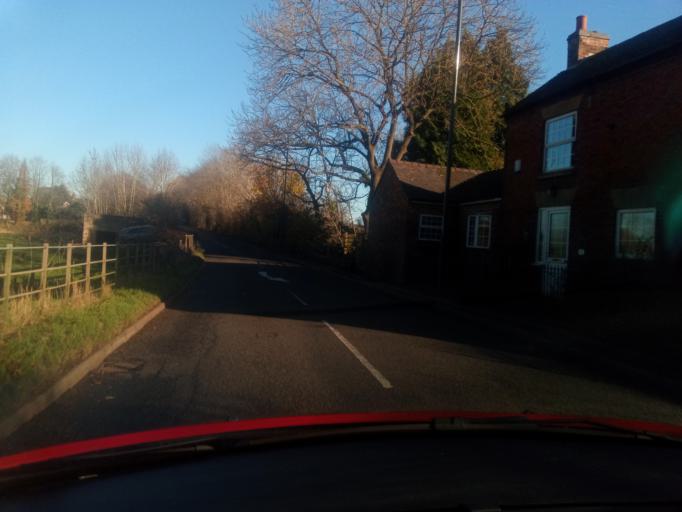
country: GB
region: England
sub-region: Derbyshire
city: Duffield
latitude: 53.0171
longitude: -1.5494
